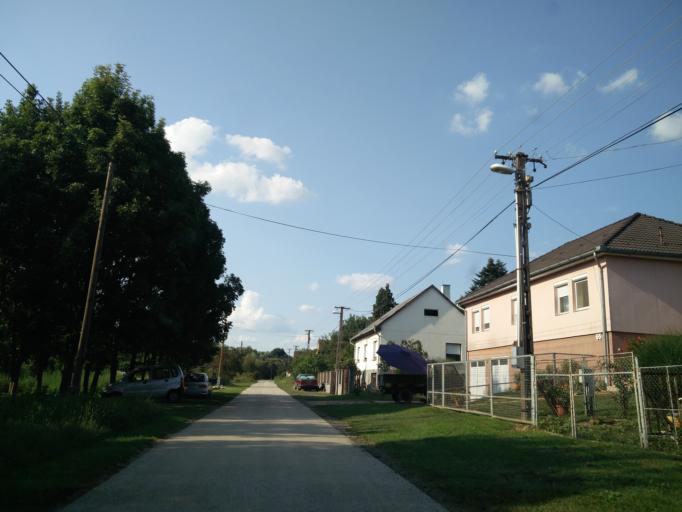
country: HU
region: Zala
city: Zalaegerszeg
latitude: 46.8682
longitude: 16.8496
